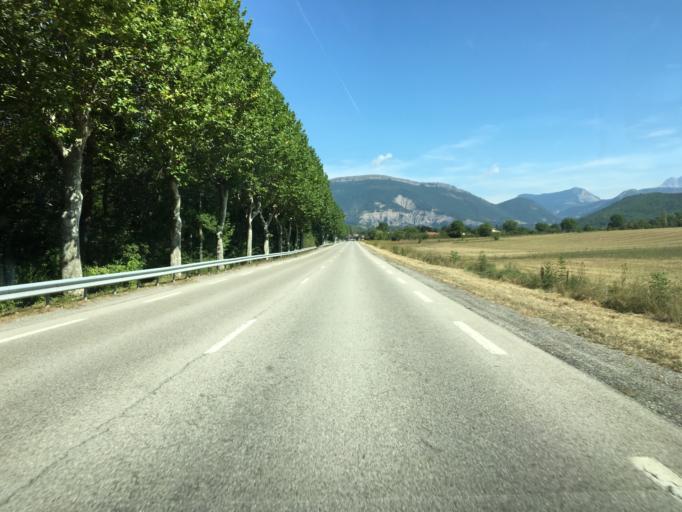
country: FR
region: Provence-Alpes-Cote d'Azur
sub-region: Departement des Hautes-Alpes
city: Serres
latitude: 44.4830
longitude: 5.7282
